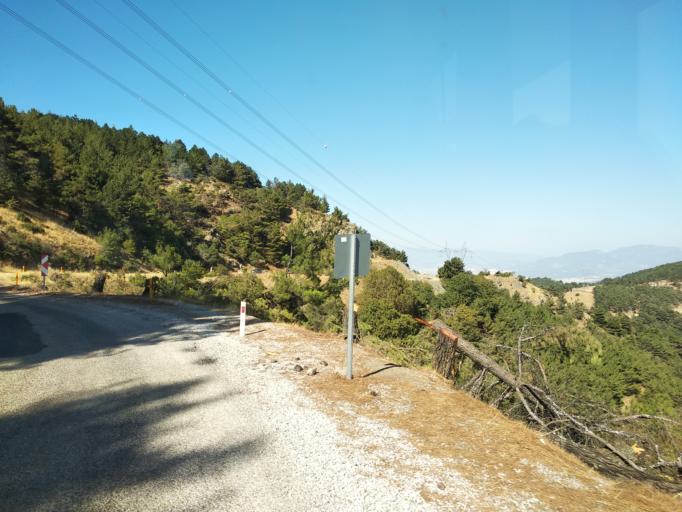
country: TR
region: Izmir
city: Gaziemir
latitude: 38.3140
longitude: 27.0059
